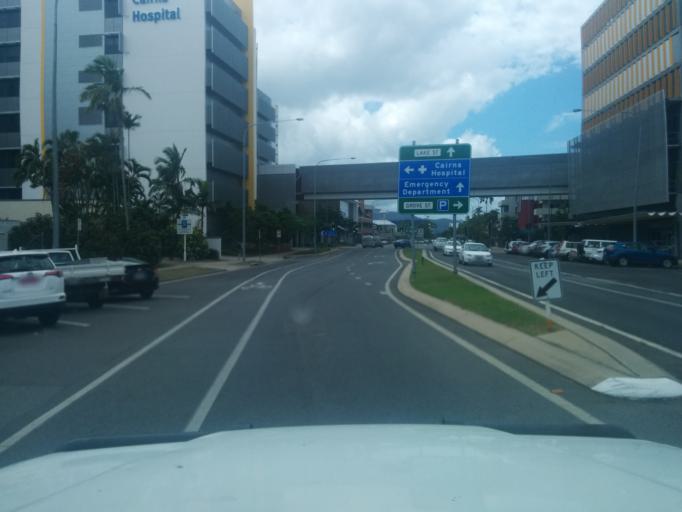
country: AU
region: Queensland
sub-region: Cairns
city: Cairns
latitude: -16.9113
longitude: 145.7664
